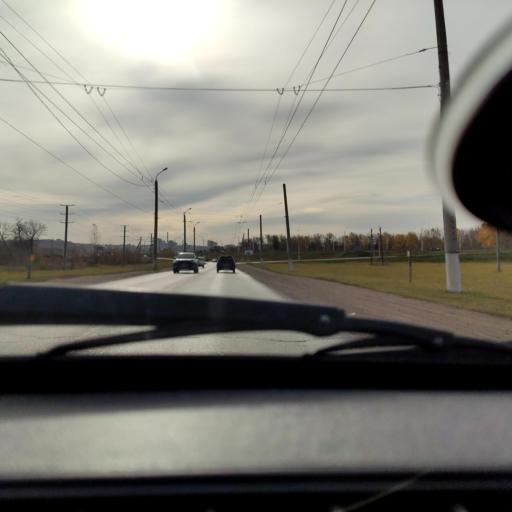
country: RU
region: Bashkortostan
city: Ufa
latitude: 54.7792
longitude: 55.9487
